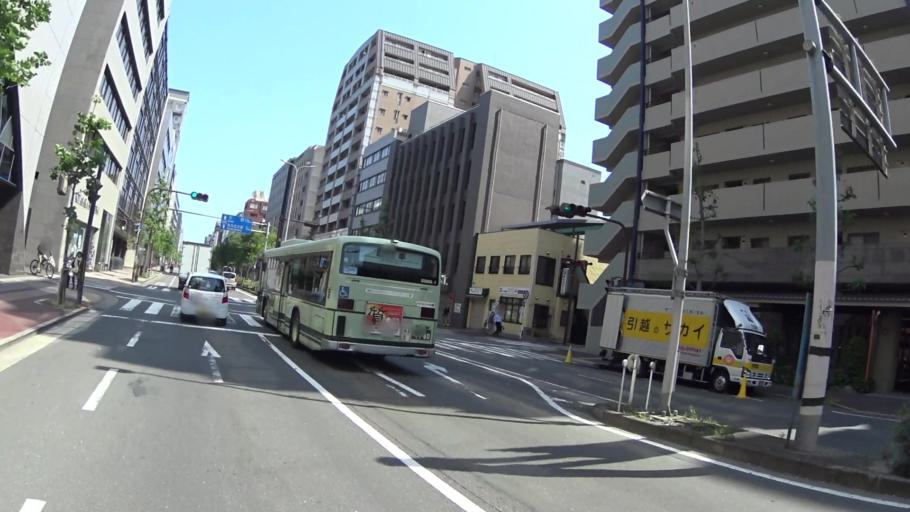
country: JP
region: Kyoto
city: Kyoto
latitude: 34.9976
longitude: 135.7593
